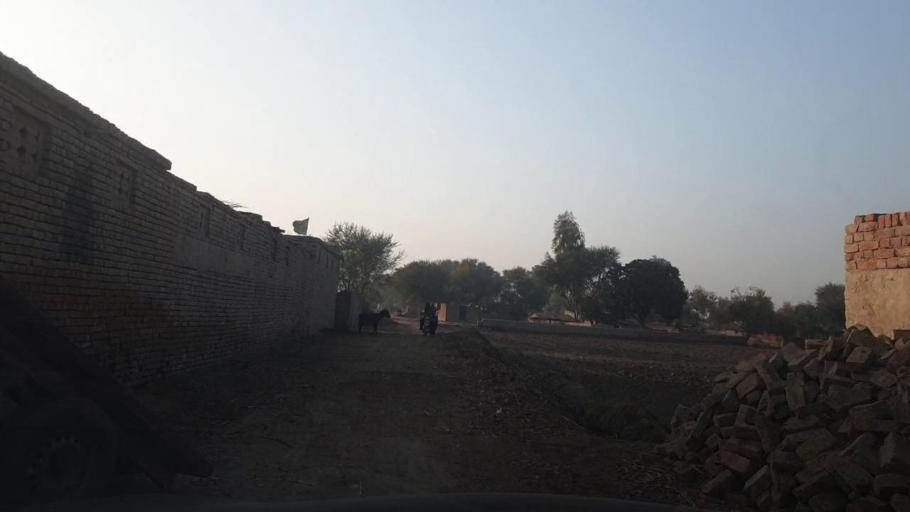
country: PK
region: Sindh
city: Ubauro
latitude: 28.3304
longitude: 69.7748
